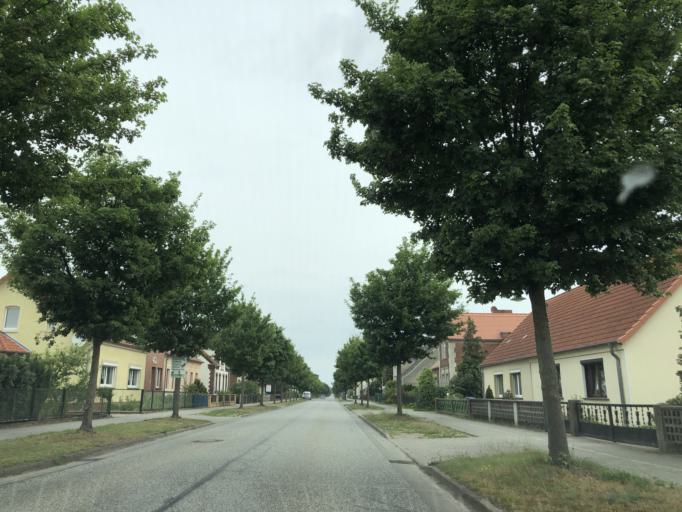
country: DE
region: Saxony-Anhalt
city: Havelberg
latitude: 52.9051
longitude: 12.0851
